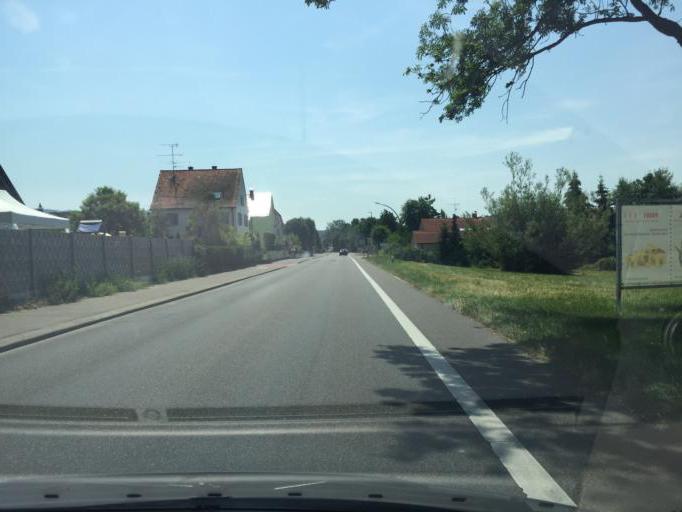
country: DE
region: Baden-Wuerttemberg
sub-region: Freiburg Region
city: Rielasingen-Worblingen
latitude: 47.7389
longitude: 8.8410
